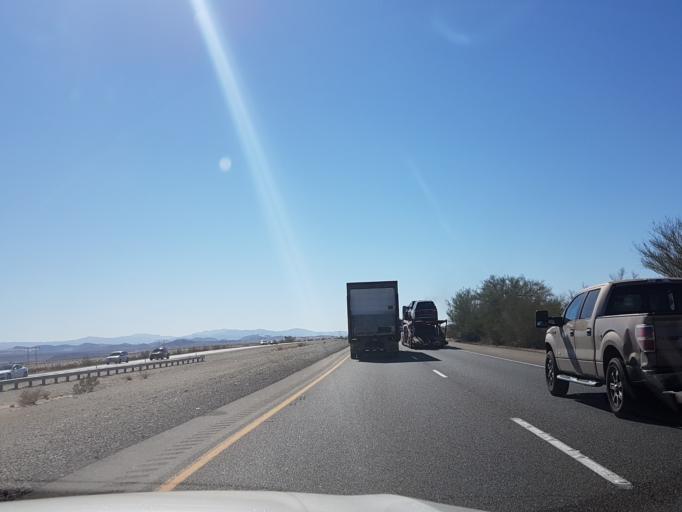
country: US
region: California
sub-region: San Bernardino County
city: Fort Irwin
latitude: 35.0471
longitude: -116.4491
